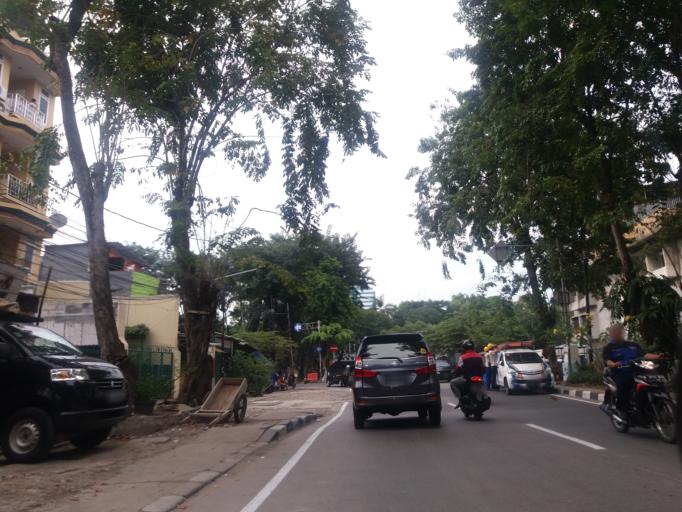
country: ID
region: Jakarta Raya
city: Jakarta
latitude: -6.1454
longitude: 106.8319
